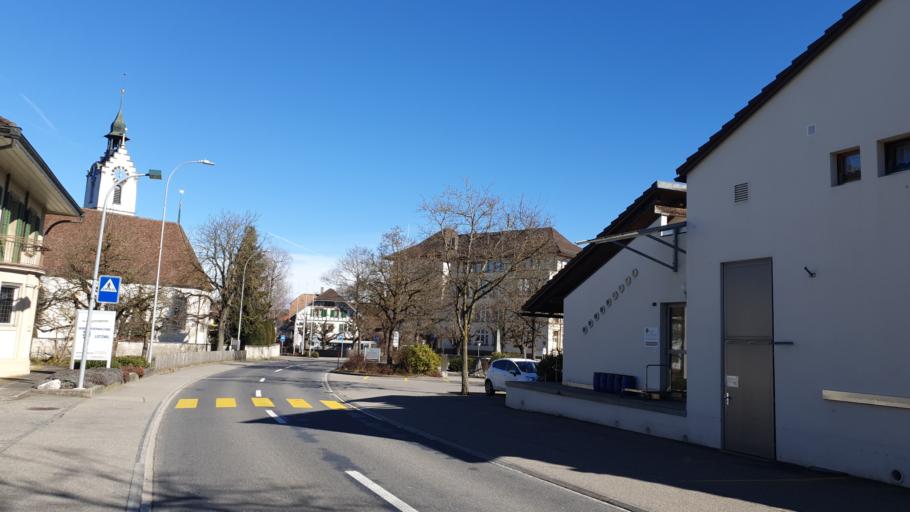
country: CH
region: Bern
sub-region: Oberaargau
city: Lotzwil
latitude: 47.1899
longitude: 7.7895
